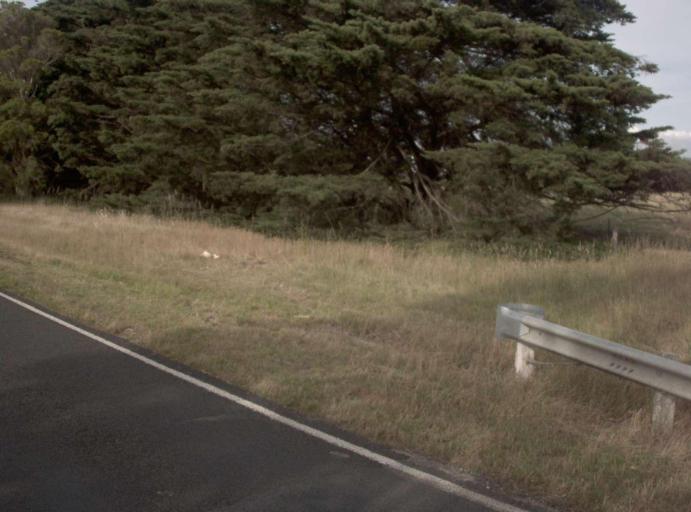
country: AU
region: Victoria
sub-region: Wellington
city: Heyfield
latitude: -38.0203
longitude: 146.6700
